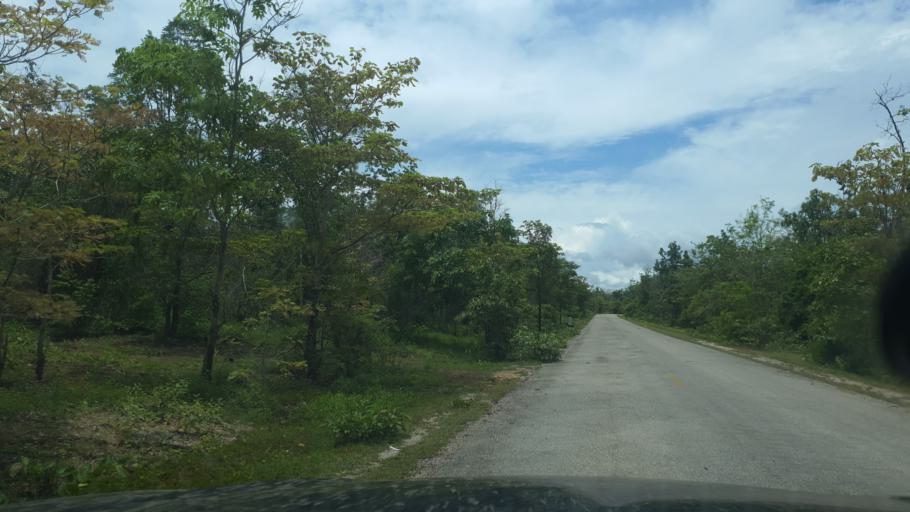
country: TH
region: Lampang
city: Soem Ngam
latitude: 18.0544
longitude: 99.3624
